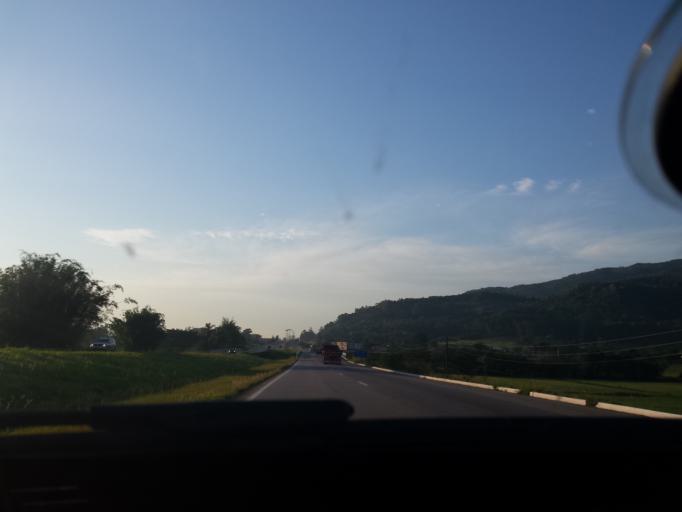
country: BR
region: Santa Catarina
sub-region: Imbituba
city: Imbituba
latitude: -28.0584
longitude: -48.7176
